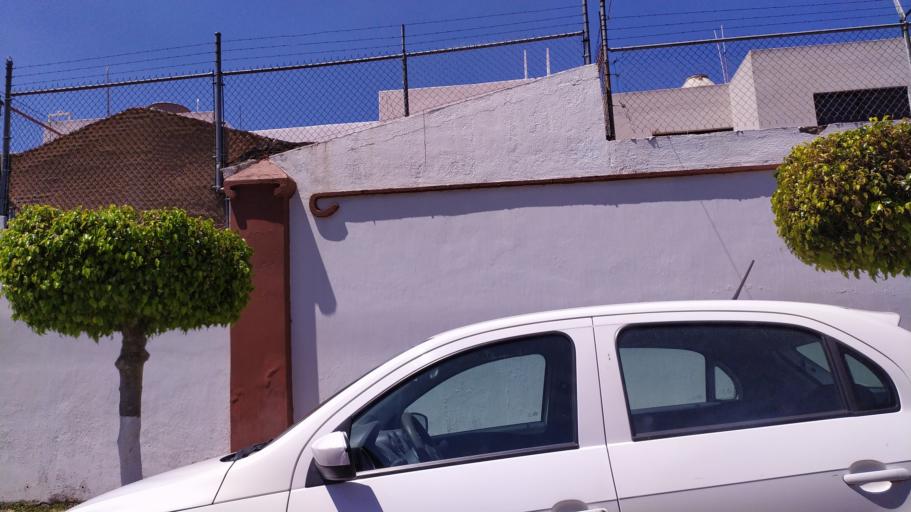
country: MX
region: Jalisco
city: Zapopan2
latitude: 20.6923
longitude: -103.4358
